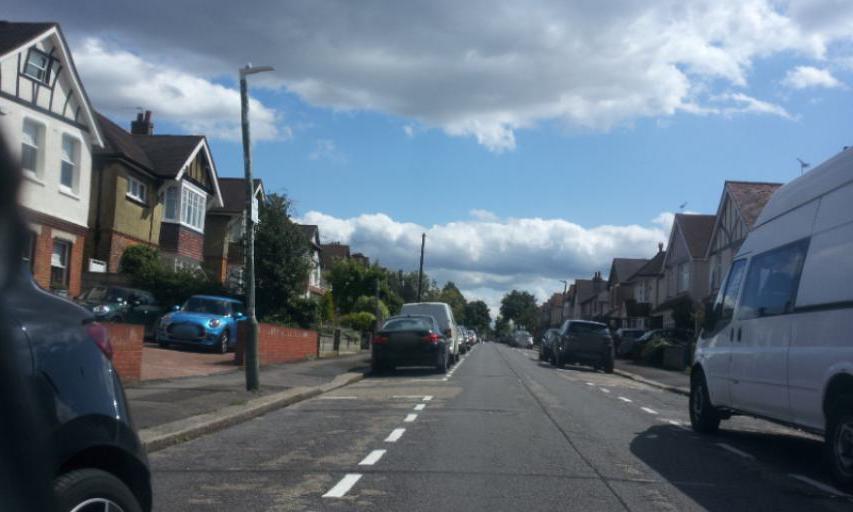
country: GB
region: England
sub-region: Kent
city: Maidstone
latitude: 51.2827
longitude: 0.5283
